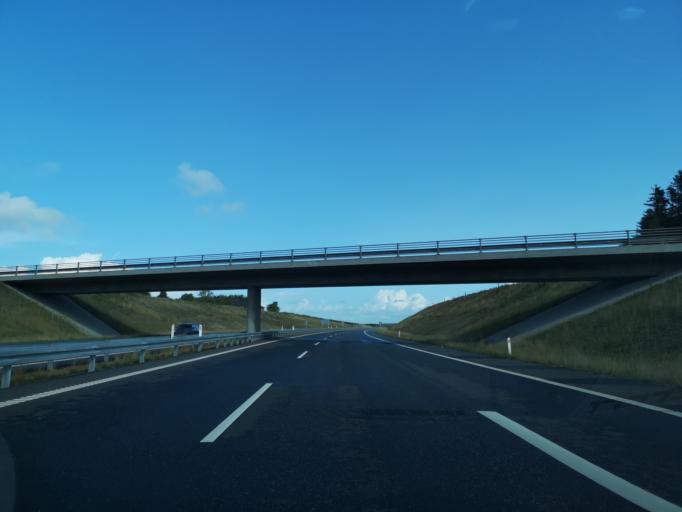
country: DK
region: Central Jutland
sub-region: Herning Kommune
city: Snejbjerg
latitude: 56.1338
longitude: 8.8708
